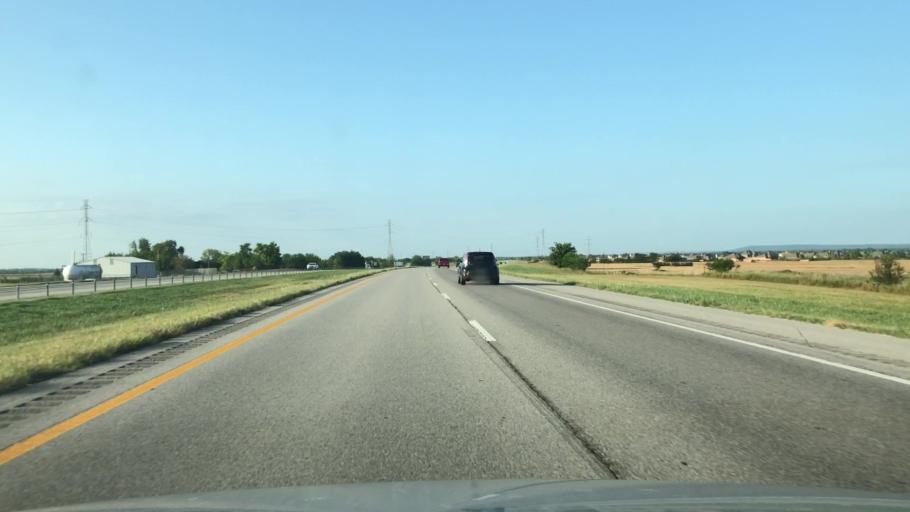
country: US
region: Oklahoma
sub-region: Osage County
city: Skiatook
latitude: 36.3521
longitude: -95.9210
